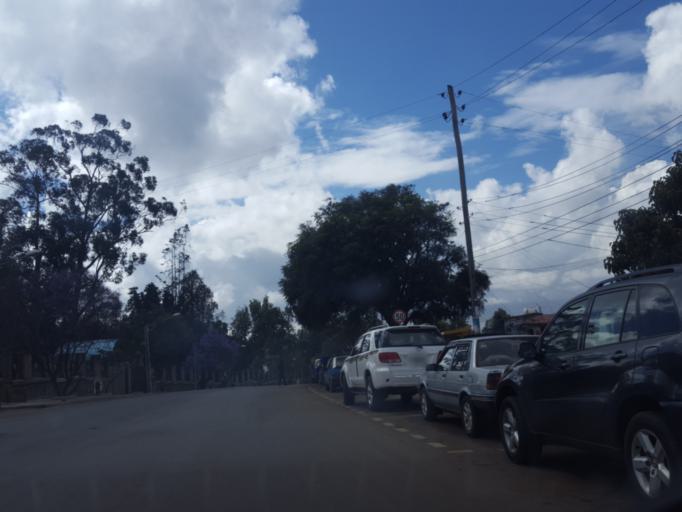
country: ET
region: Adis Abeba
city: Addis Ababa
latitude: 9.0572
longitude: 38.7627
